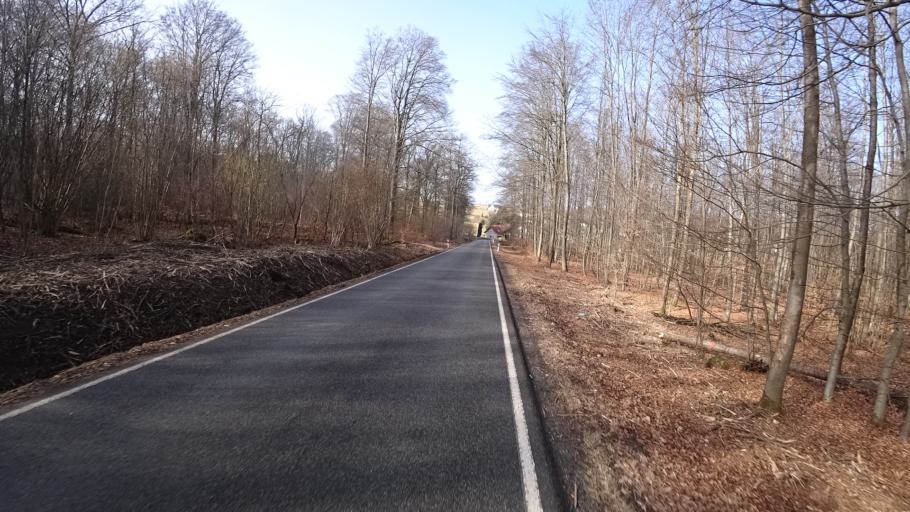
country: DE
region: Rheinland-Pfalz
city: Dickendorf
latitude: 50.7297
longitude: 7.8506
